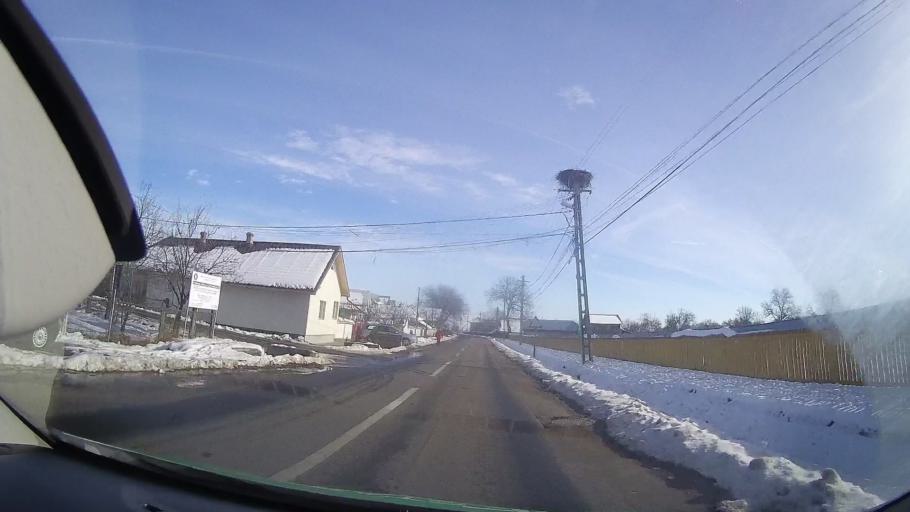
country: RO
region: Neamt
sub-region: Comuna Agapia
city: Agapia
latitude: 47.1733
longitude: 26.2855
